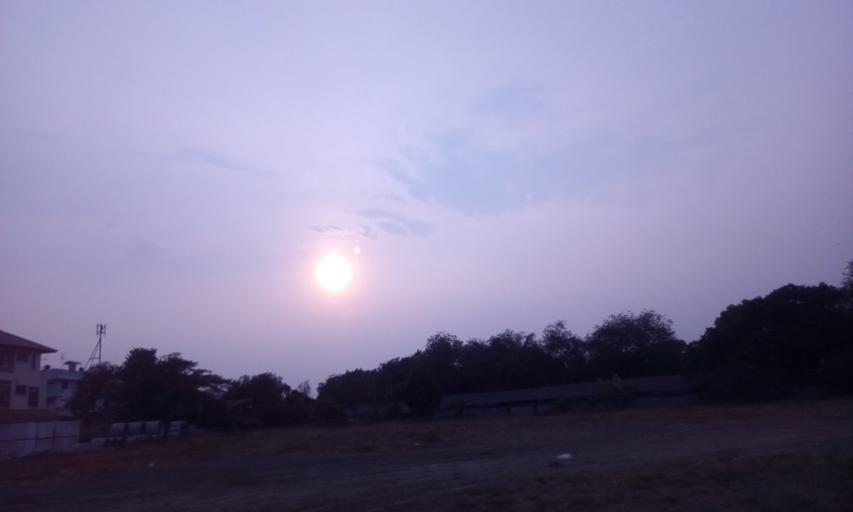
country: TH
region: Bangkok
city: Nong Chok
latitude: 13.8581
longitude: 100.8682
